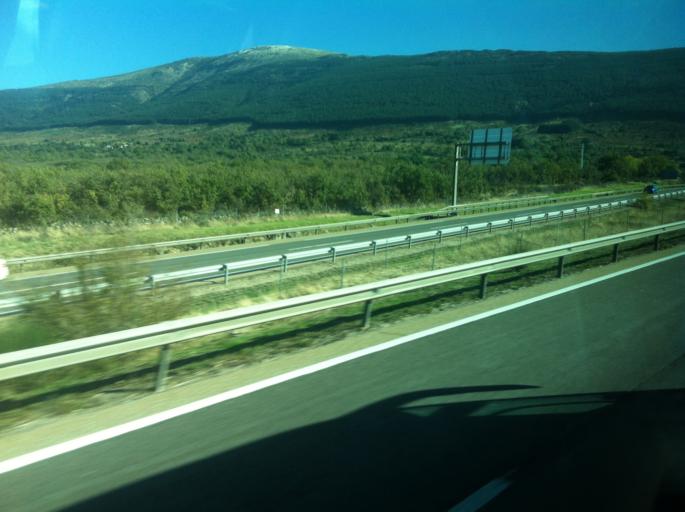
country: ES
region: Castille and Leon
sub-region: Provincia de Segovia
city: Cerezo de Abajo
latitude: 41.1797
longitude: -3.5835
